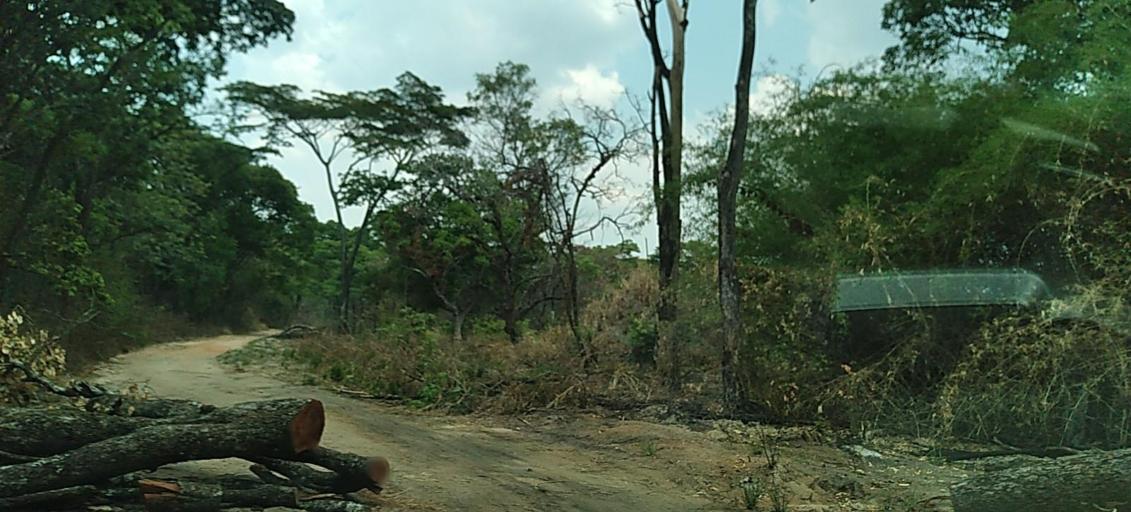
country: ZM
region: Copperbelt
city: Chingola
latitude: -12.7562
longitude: 27.7076
